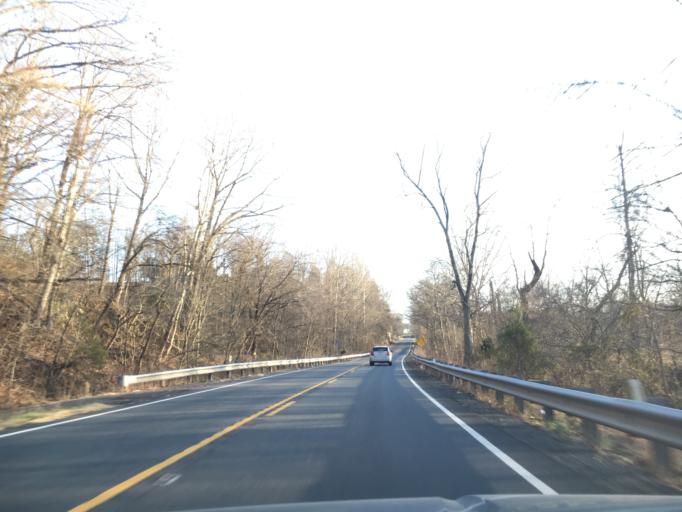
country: US
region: Virginia
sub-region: Culpeper County
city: Merrimac
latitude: 38.5312
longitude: -78.1194
